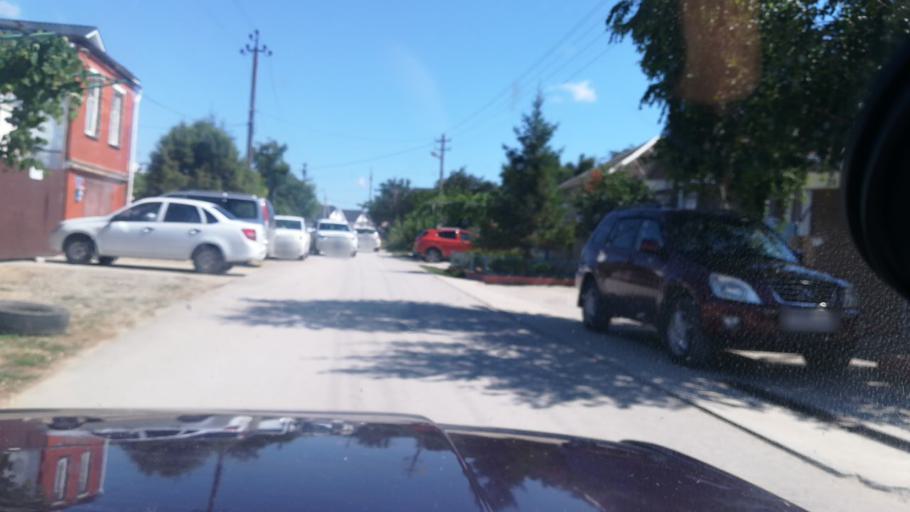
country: RU
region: Krasnodarskiy
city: Vityazevo
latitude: 44.9926
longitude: 37.2746
